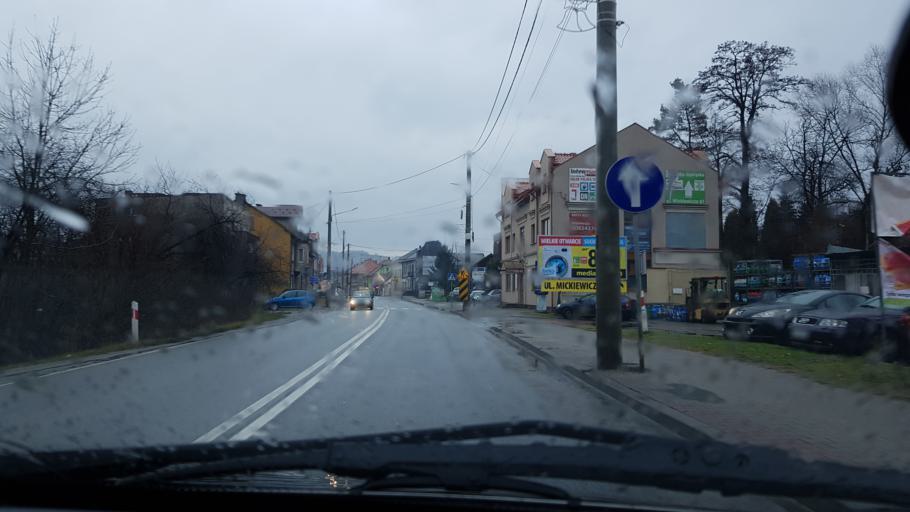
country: PL
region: Lesser Poland Voivodeship
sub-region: Powiat suski
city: Sucha Beskidzka
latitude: 49.7384
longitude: 19.5750
